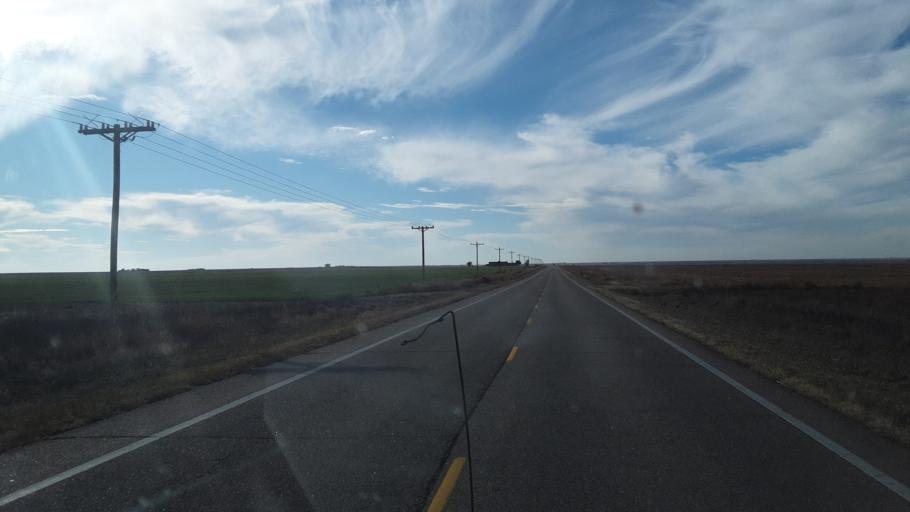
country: US
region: Kansas
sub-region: Gray County
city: Cimarron
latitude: 38.0592
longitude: -100.4897
